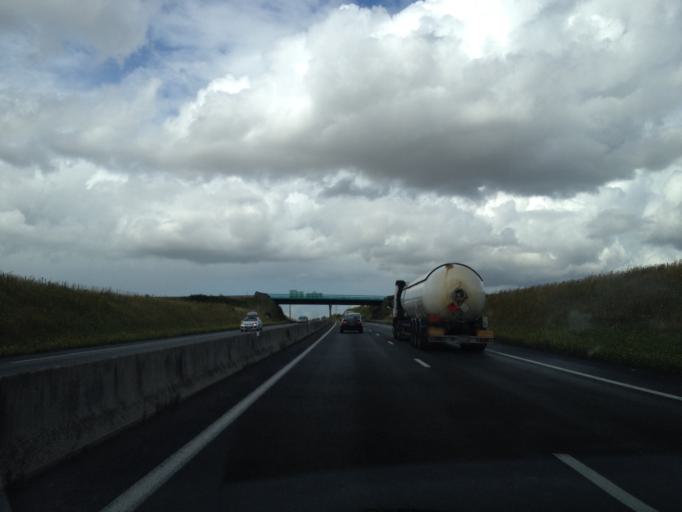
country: FR
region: Picardie
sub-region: Departement de la Somme
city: Sailly-Flibeaucourt
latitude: 50.1487
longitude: 1.7985
